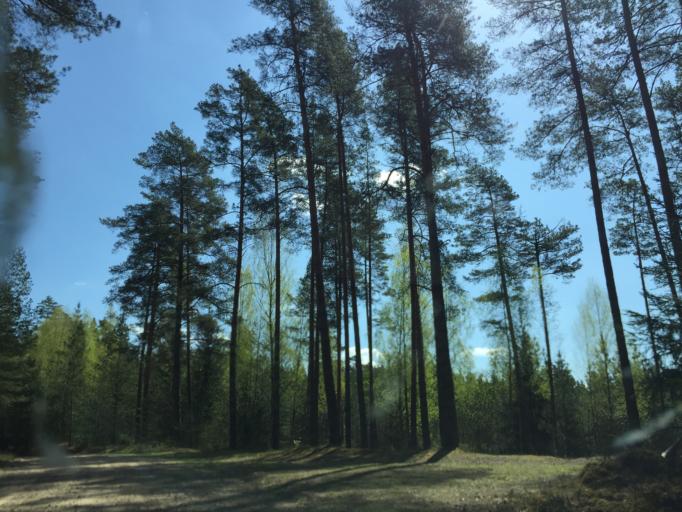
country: LV
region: Vecumnieki
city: Vecumnieki
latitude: 56.6508
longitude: 24.4730
